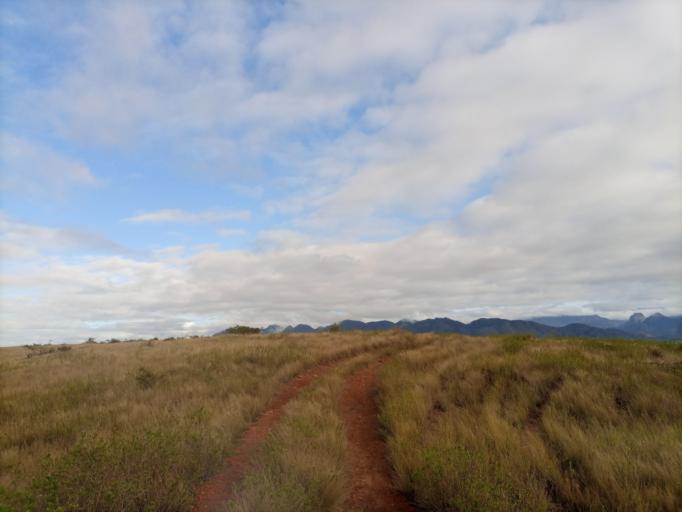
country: MG
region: Anosy
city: Fort Dauphin
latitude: -24.3138
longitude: 47.2533
